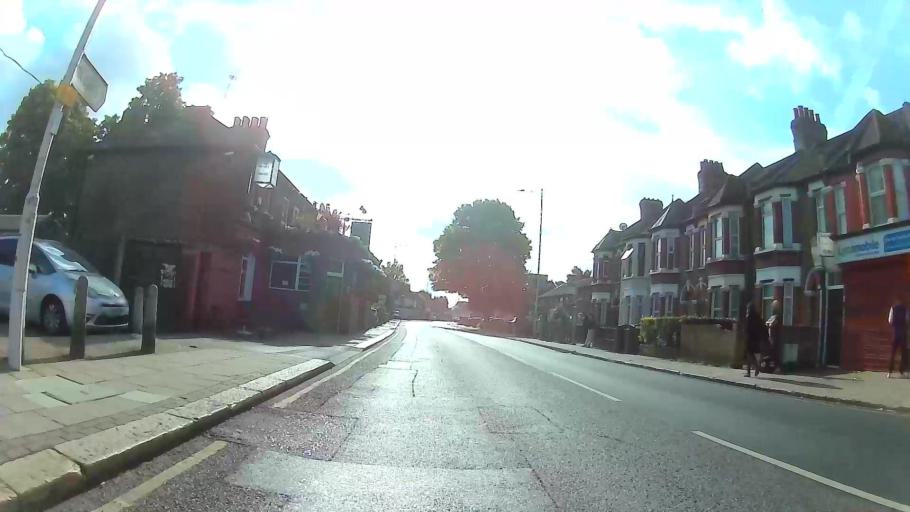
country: GB
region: England
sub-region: Greater London
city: Ilford
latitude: 51.5590
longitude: 0.0856
